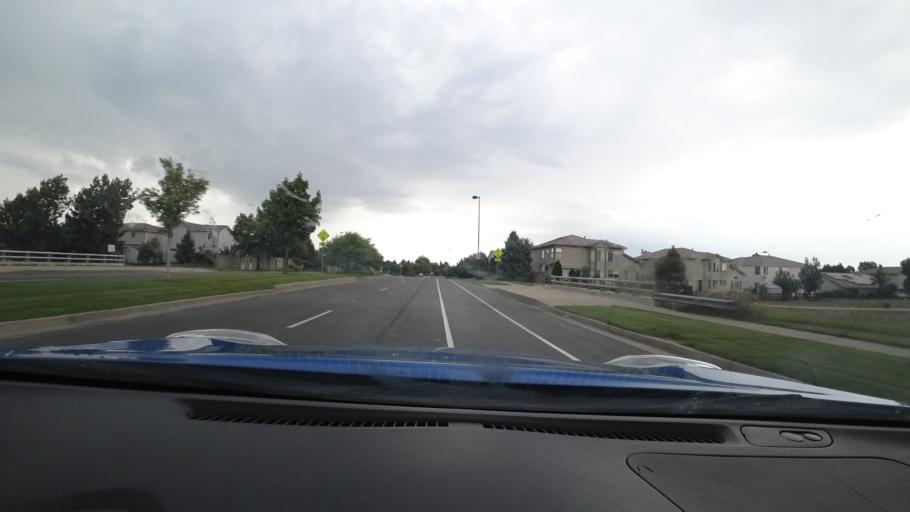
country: US
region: Colorado
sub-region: Adams County
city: Aurora
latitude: 39.7781
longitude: -104.7545
